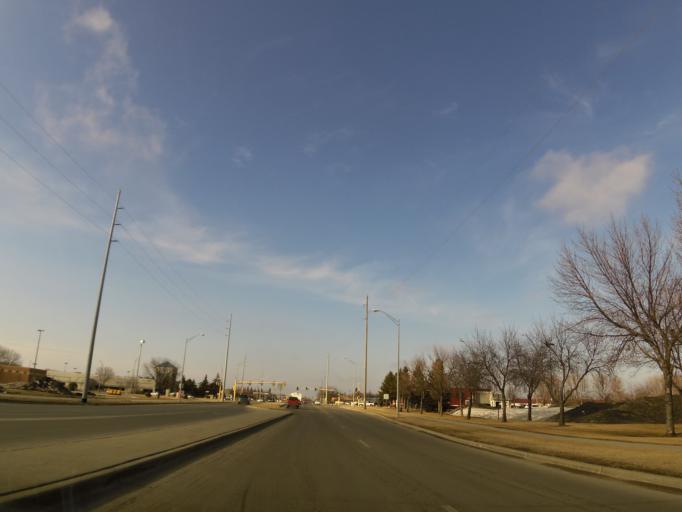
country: US
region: North Dakota
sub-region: Grand Forks County
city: Grand Forks
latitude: 47.8878
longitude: -97.0666
